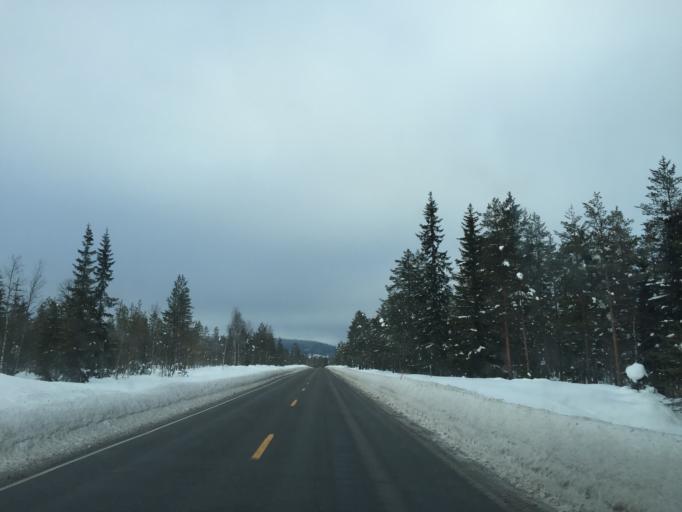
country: NO
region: Hedmark
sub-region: Trysil
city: Innbygda
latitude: 61.1502
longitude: 12.1304
